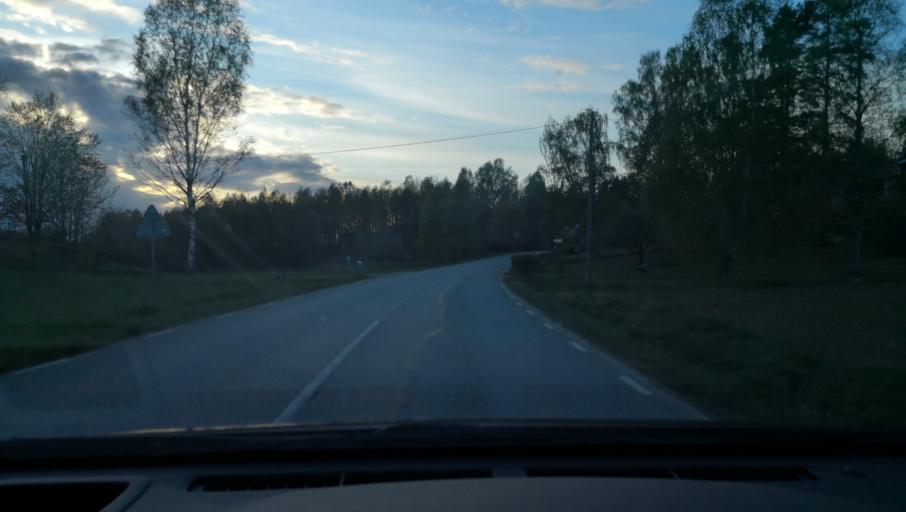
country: SE
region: OErebro
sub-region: Askersunds Kommun
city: Asbro
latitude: 58.9333
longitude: 15.0227
